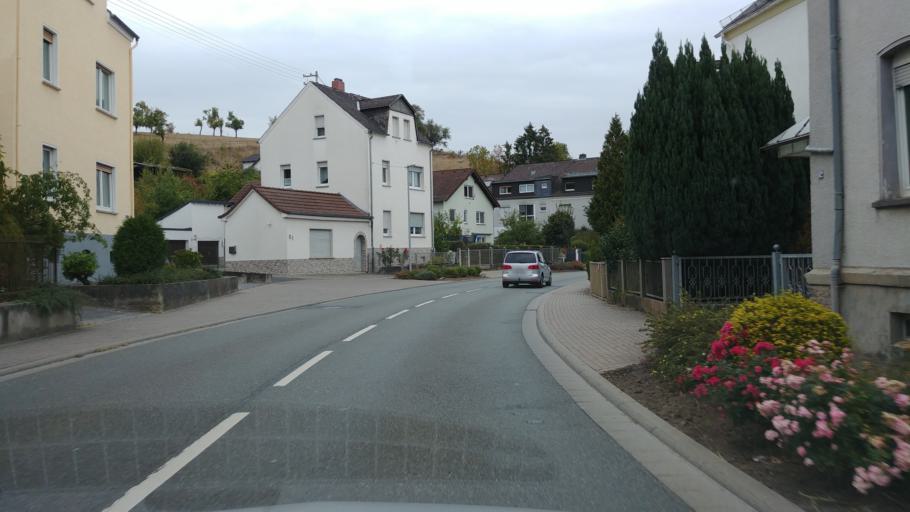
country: DE
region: Rheinland-Pfalz
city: Holzheim
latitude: 50.3463
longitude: 8.0478
